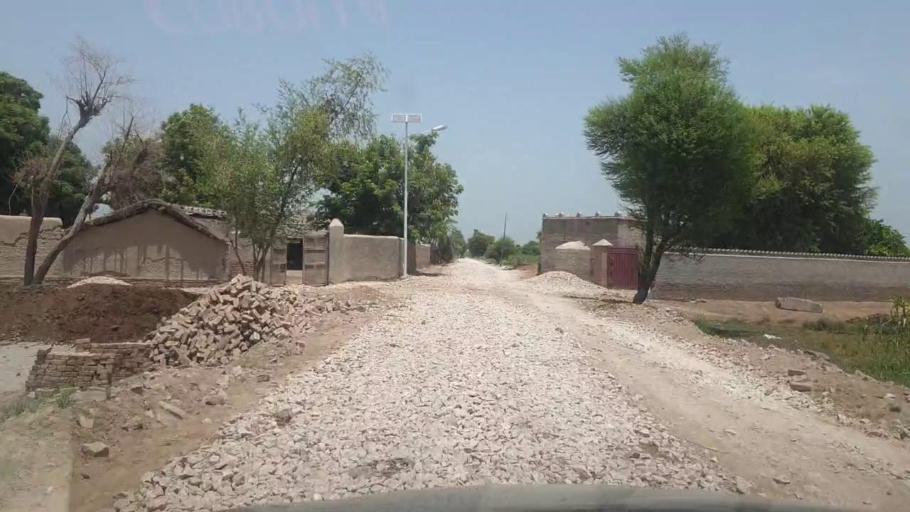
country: PK
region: Sindh
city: Sobhadero
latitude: 27.3268
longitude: 68.3528
